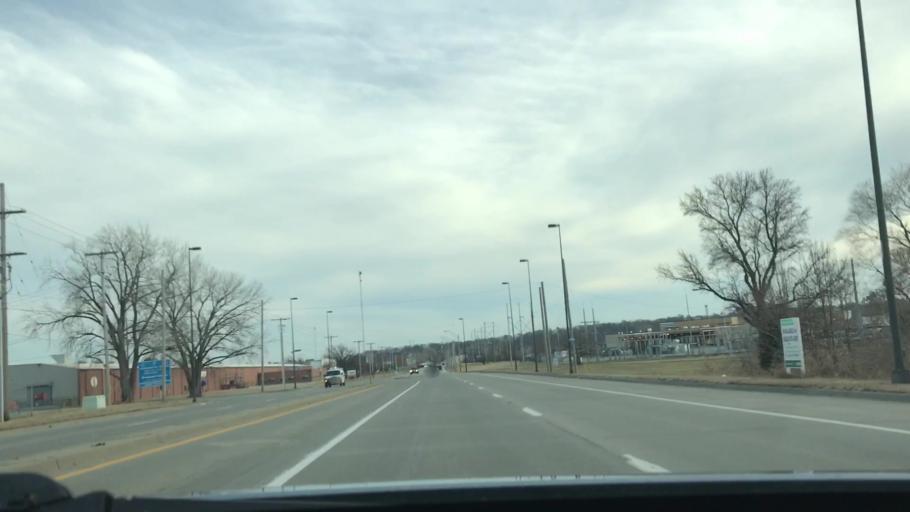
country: US
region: Missouri
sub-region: Clay County
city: North Kansas City
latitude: 39.1367
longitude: -94.5281
